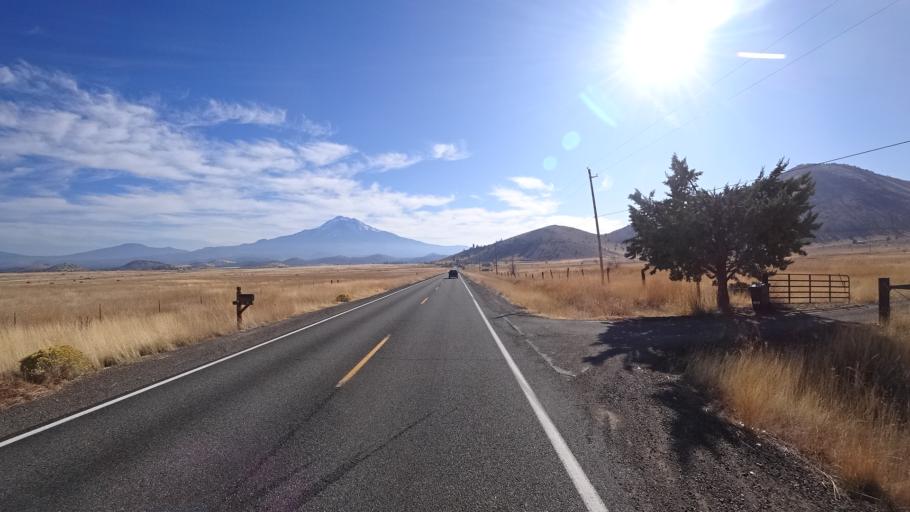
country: US
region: California
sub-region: Siskiyou County
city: Weed
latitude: 41.4745
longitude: -122.4834
